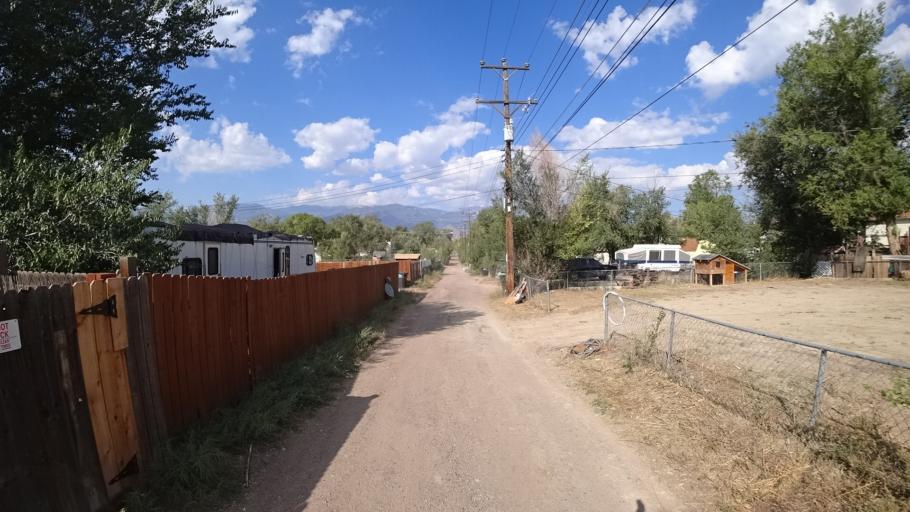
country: US
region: Colorado
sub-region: El Paso County
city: Colorado Springs
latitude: 38.8233
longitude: -104.8062
